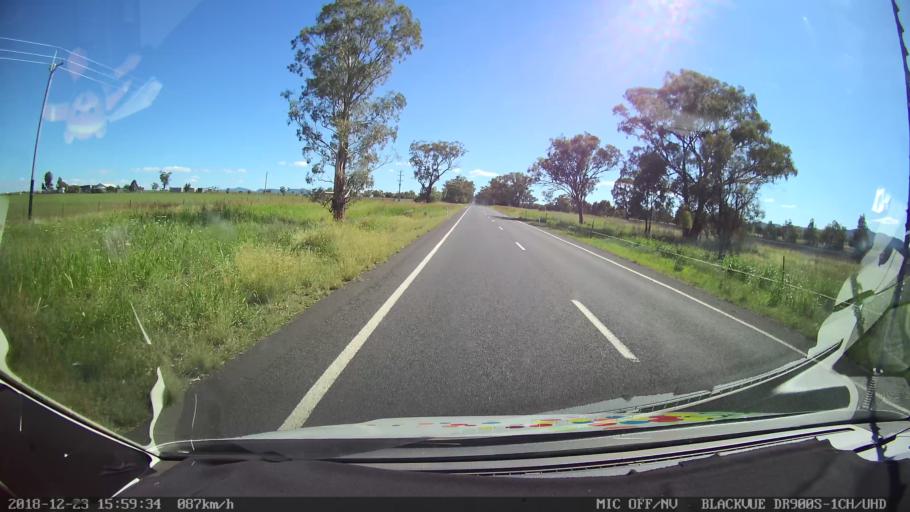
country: AU
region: New South Wales
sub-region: Tamworth Municipality
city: Phillip
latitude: -31.2011
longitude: 150.8322
